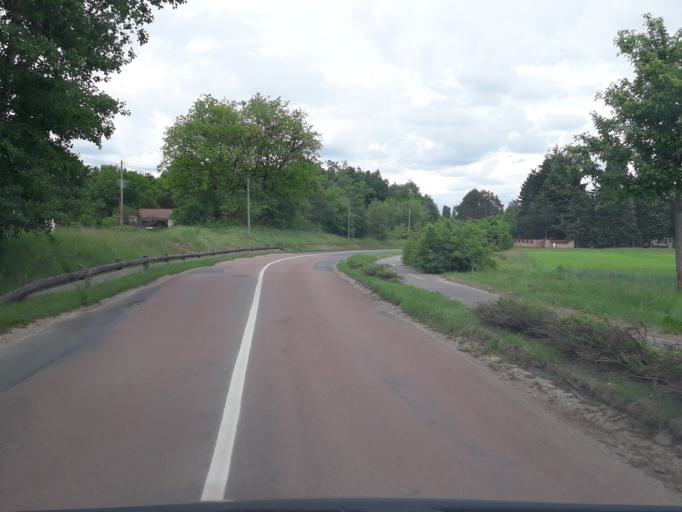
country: FR
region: Ile-de-France
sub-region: Departement de l'Essonne
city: Boissy-le-Cutte
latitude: 48.4362
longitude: 2.2883
